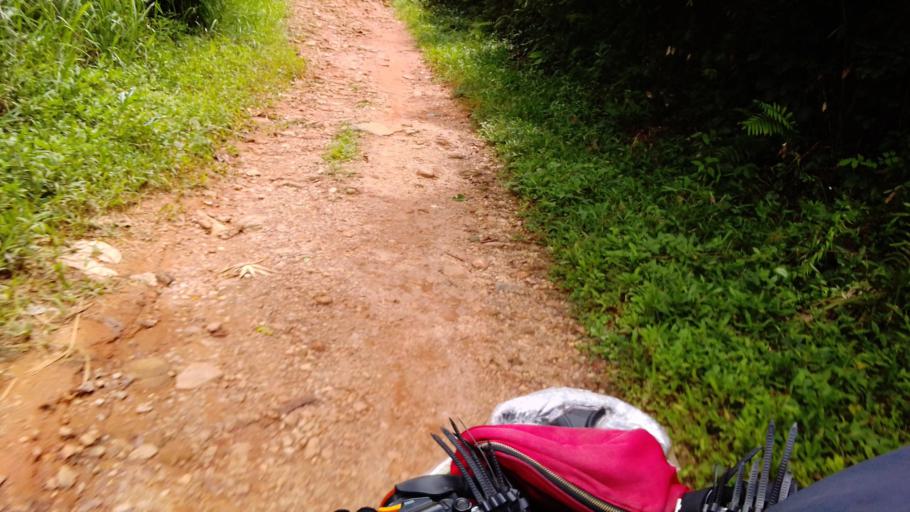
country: SL
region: Eastern Province
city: Koyima
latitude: 8.6803
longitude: -11.0061
